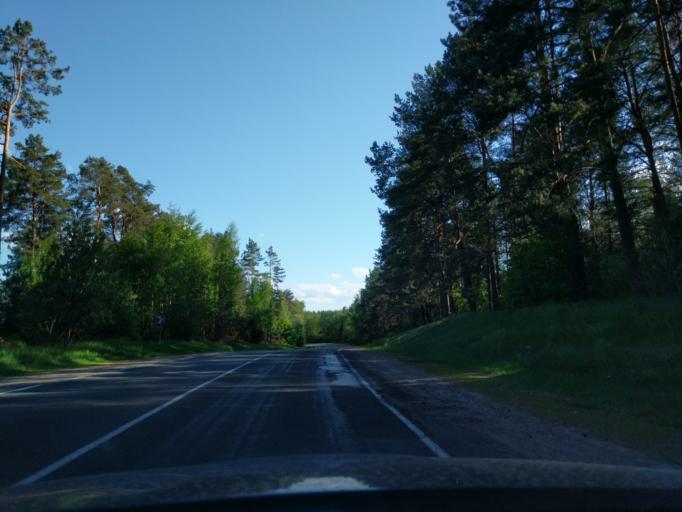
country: BY
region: Minsk
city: Myadzyel
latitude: 54.8462
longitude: 26.9261
